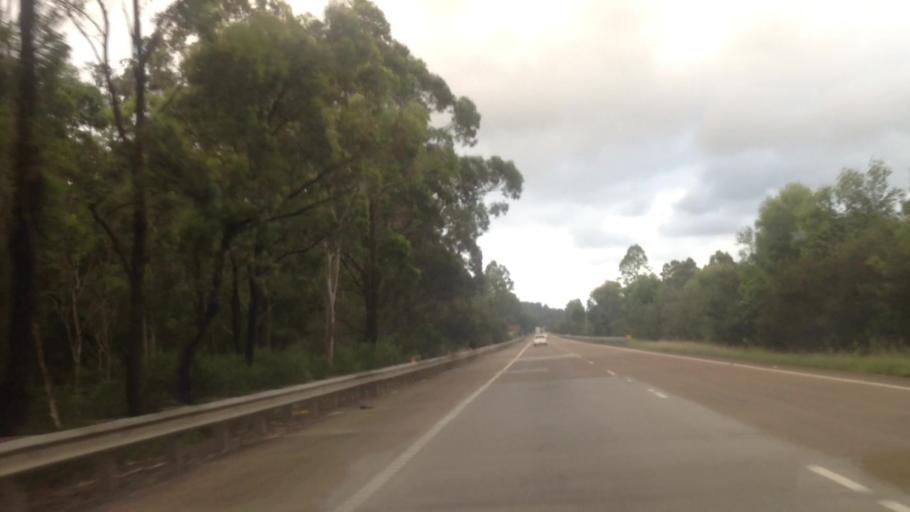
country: AU
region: New South Wales
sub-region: Wyong Shire
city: Charmhaven
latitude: -33.1676
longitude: 151.4676
